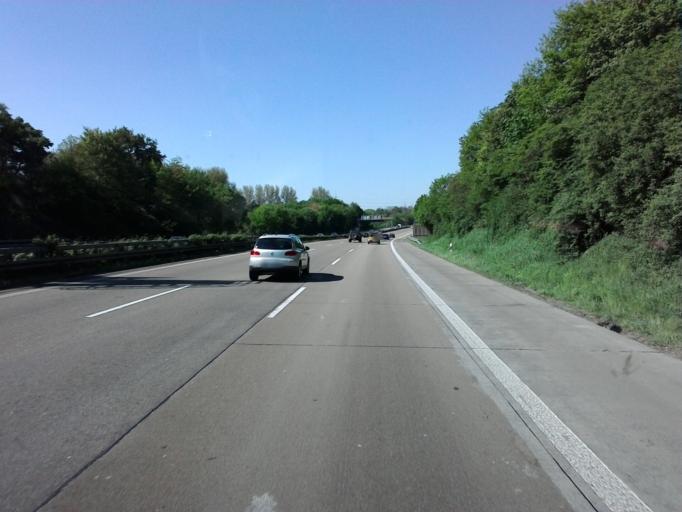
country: DE
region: North Rhine-Westphalia
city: Opladen
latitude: 51.0633
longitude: 6.9885
